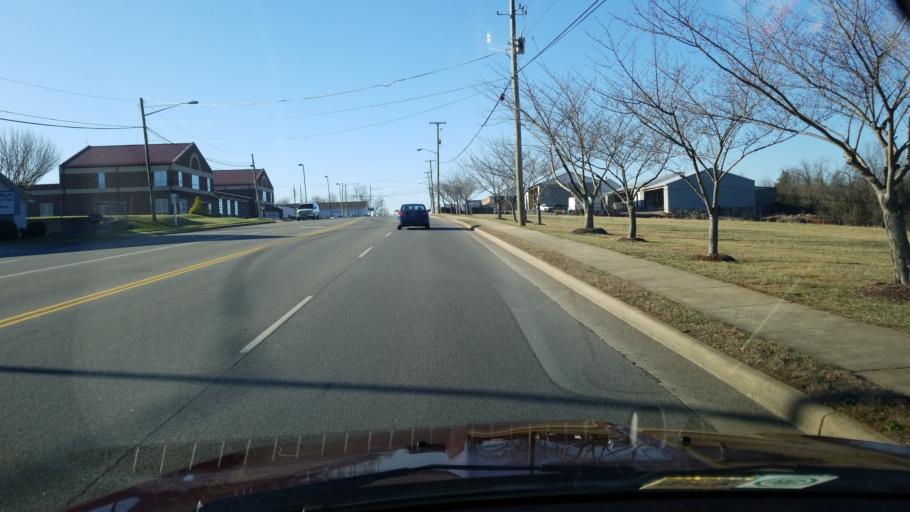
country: US
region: Virginia
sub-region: Franklin County
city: Rocky Mount
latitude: 37.0143
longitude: -79.8927
